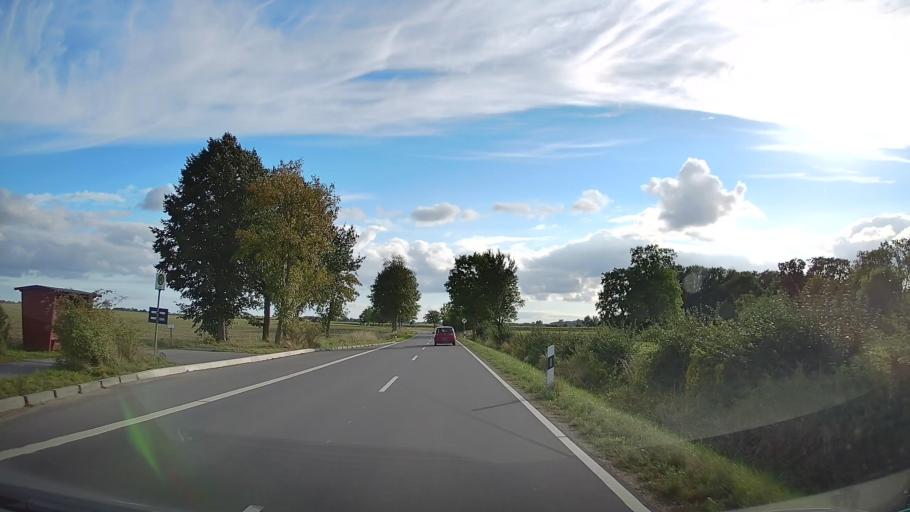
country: DE
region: Schleswig-Holstein
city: Pommerby
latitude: 54.7605
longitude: 9.9442
